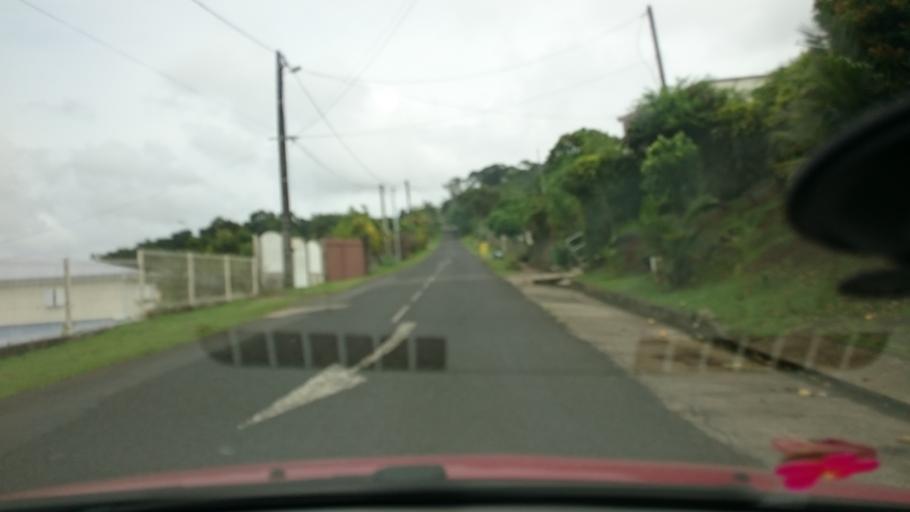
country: MQ
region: Martinique
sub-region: Martinique
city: Sainte-Luce
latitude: 14.4952
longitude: -60.9253
